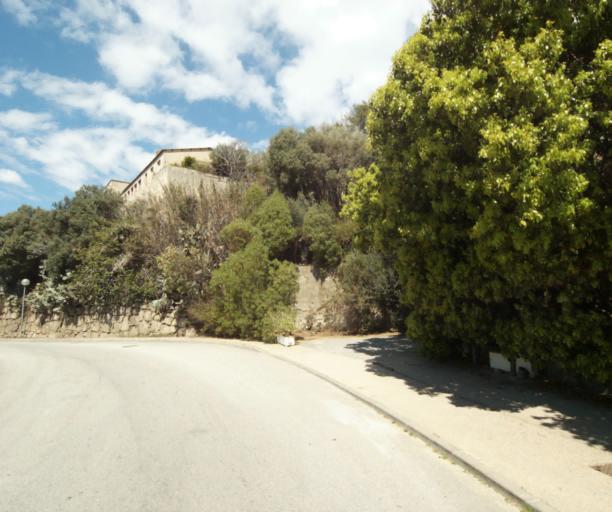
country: FR
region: Corsica
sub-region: Departement de la Corse-du-Sud
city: Propriano
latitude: 41.6724
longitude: 8.9053
